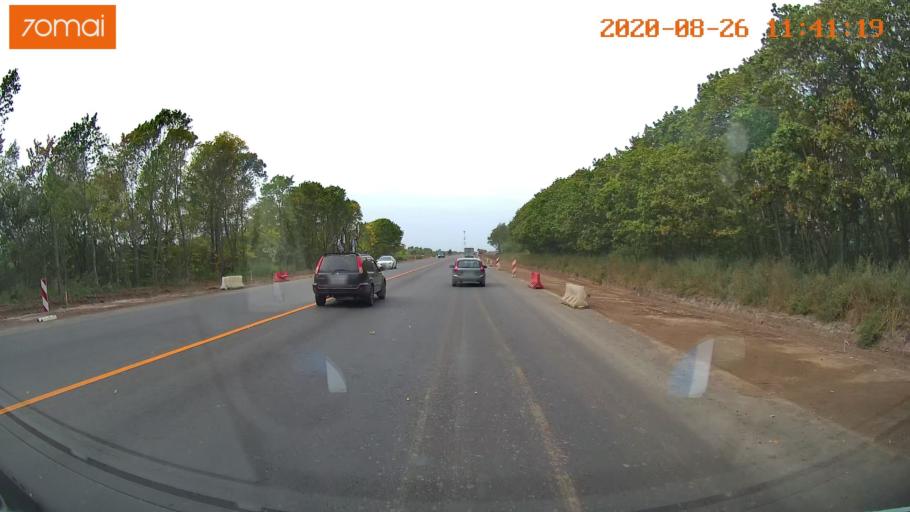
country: RU
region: Rjazan
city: Shilovo
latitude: 54.2952
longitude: 40.7136
